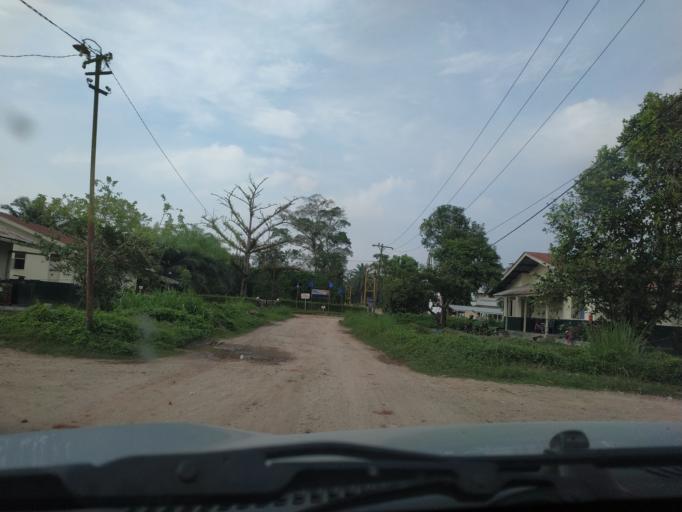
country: ID
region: North Sumatra
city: Rantauprapat
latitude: 2.3068
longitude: 100.0701
